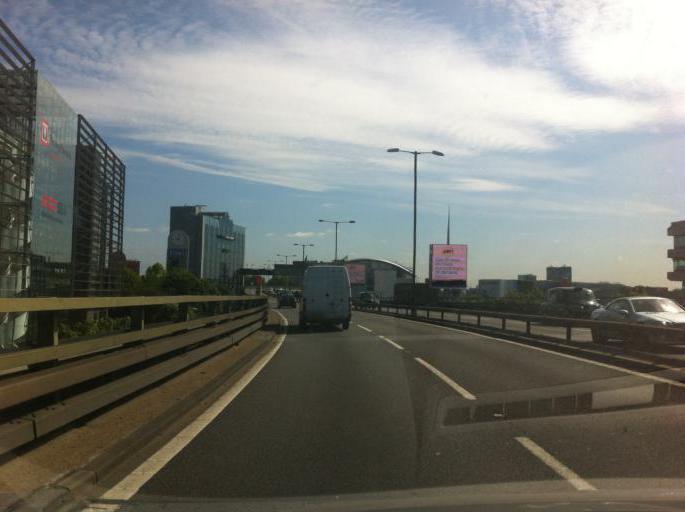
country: GB
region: England
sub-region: Greater London
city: Brentford
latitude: 51.4915
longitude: -0.2935
